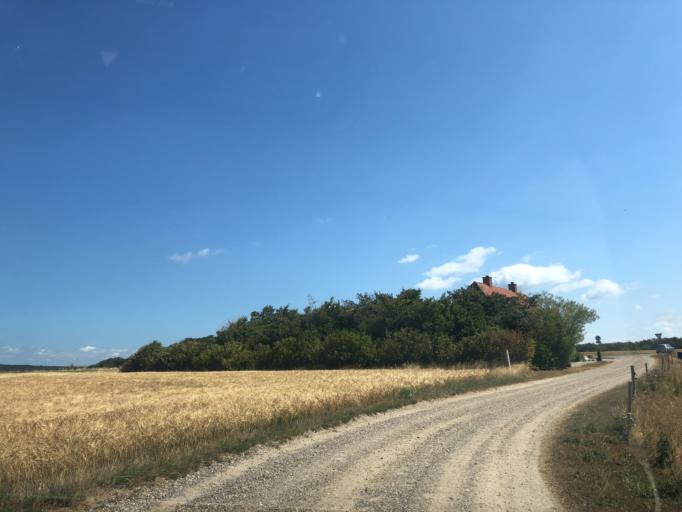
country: DK
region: North Denmark
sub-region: Morso Kommune
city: Nykobing Mors
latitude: 56.8126
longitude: 8.9933
